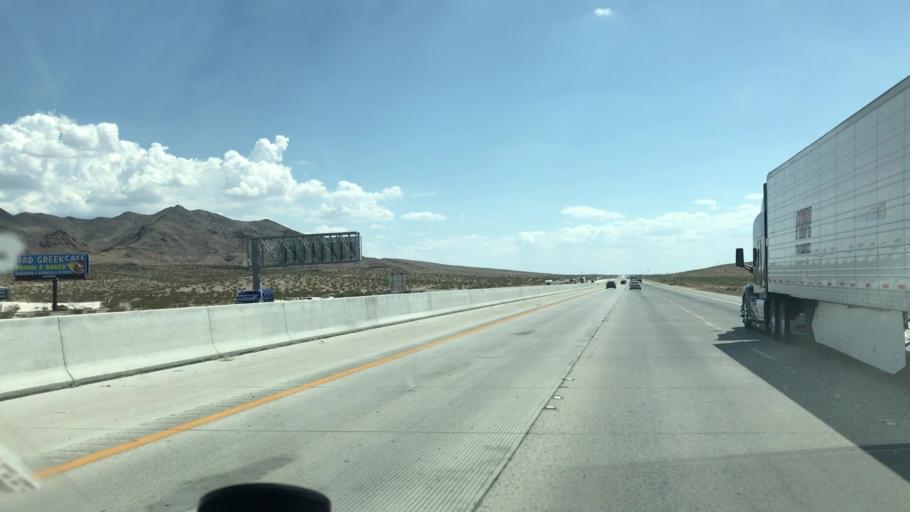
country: US
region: Nevada
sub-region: Clark County
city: Enterprise
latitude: 35.9168
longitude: -115.2029
